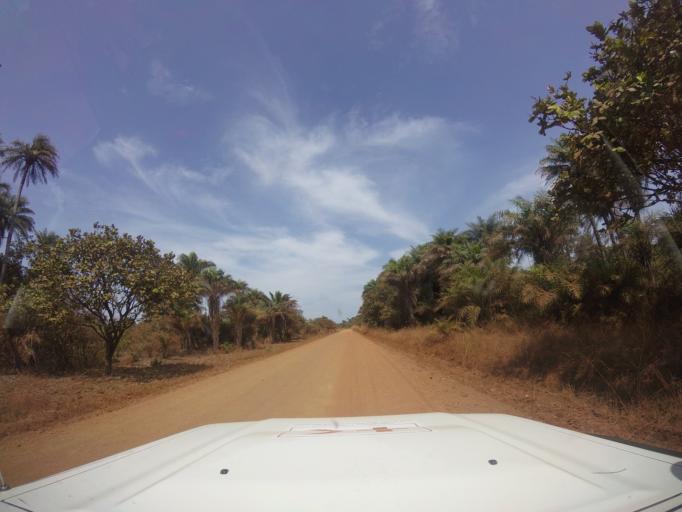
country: LR
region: Grand Cape Mount
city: Robertsport
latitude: 6.7033
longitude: -11.3122
